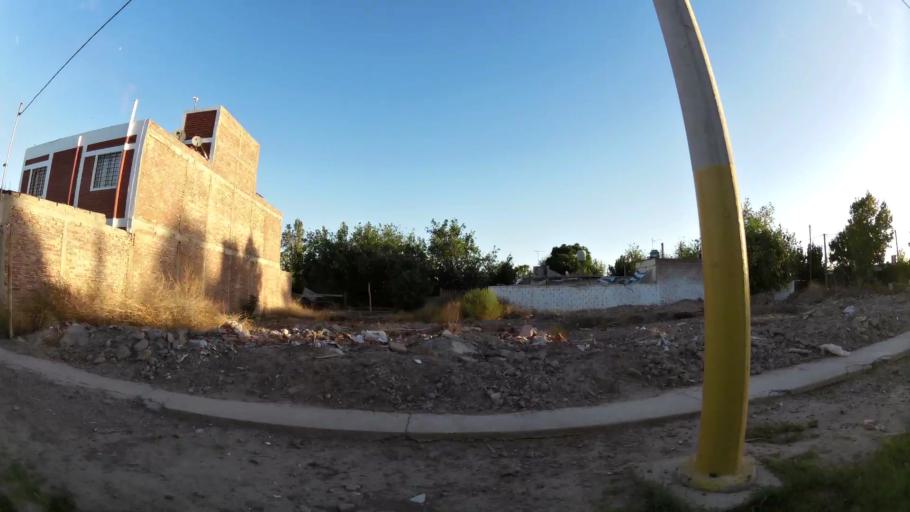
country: AR
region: San Juan
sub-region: Departamento de Santa Lucia
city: Santa Lucia
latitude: -31.5315
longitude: -68.5066
